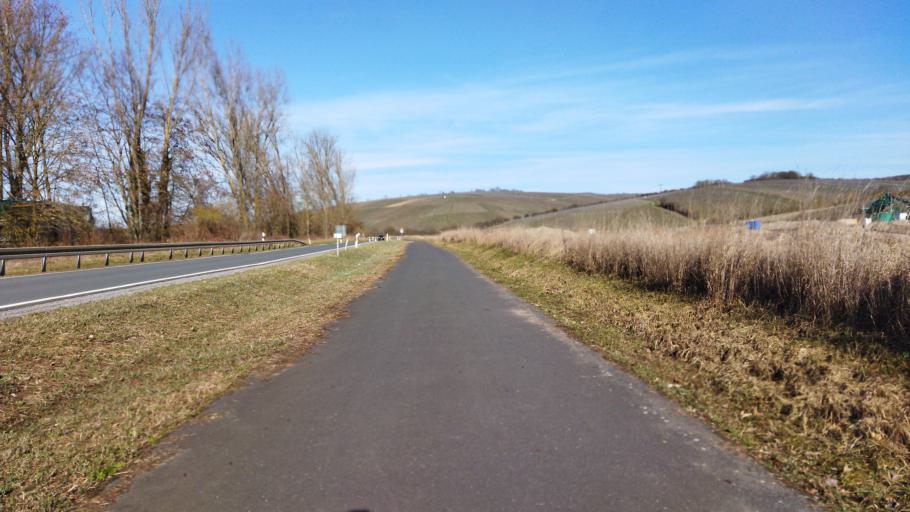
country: DE
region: Bavaria
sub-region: Regierungsbezirk Unterfranken
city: Wipfeld
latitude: 49.8905
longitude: 10.1837
